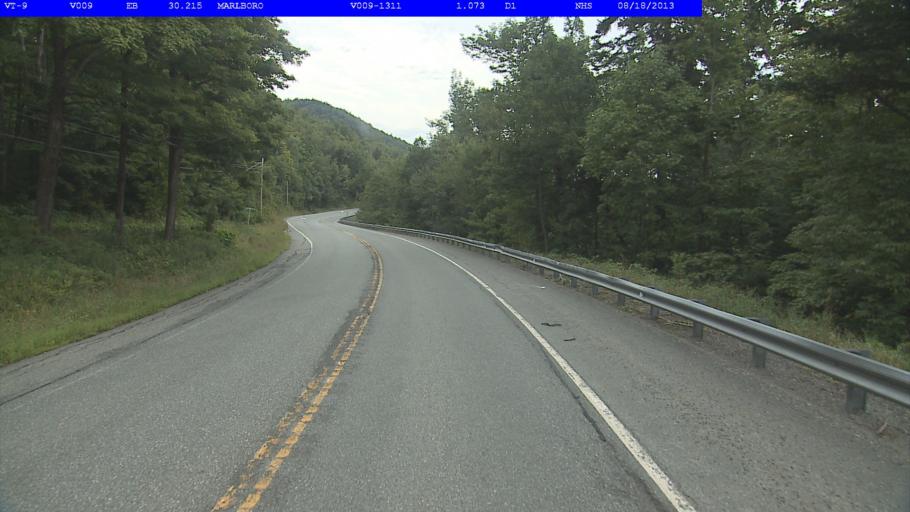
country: US
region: Vermont
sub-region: Windham County
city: Dover
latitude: 42.8570
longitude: -72.7887
